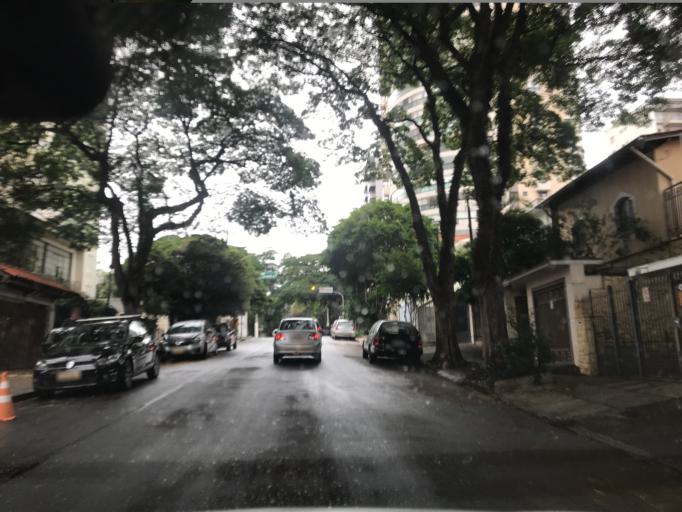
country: BR
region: Sao Paulo
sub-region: Sao Paulo
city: Sao Paulo
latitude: -23.5369
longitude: -46.6757
